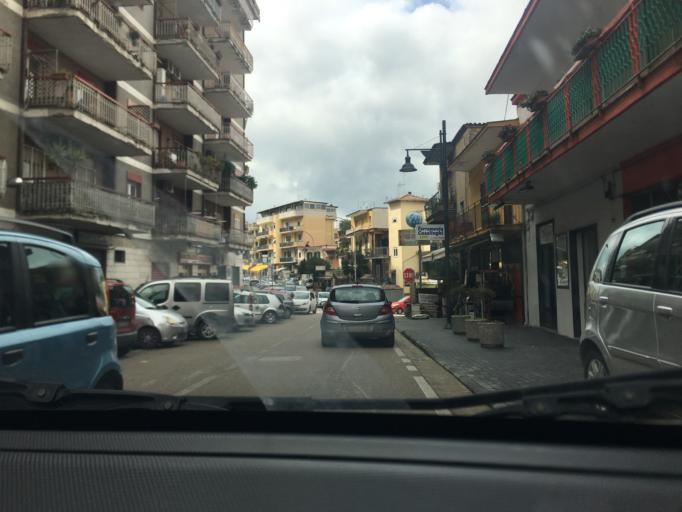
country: IT
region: Campania
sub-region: Provincia di Napoli
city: Marano di Napoli
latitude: 40.8958
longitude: 14.1837
